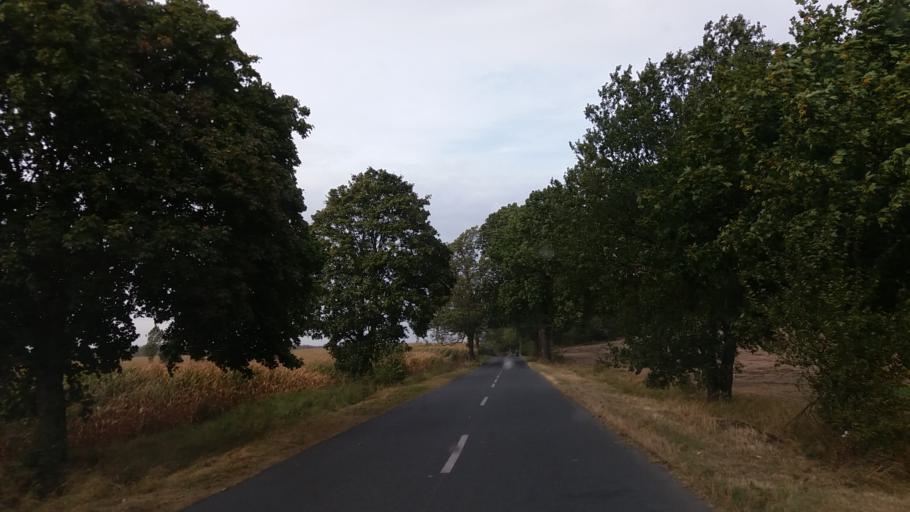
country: PL
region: West Pomeranian Voivodeship
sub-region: Powiat choszczenski
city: Krzecin
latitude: 53.0707
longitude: 15.4914
